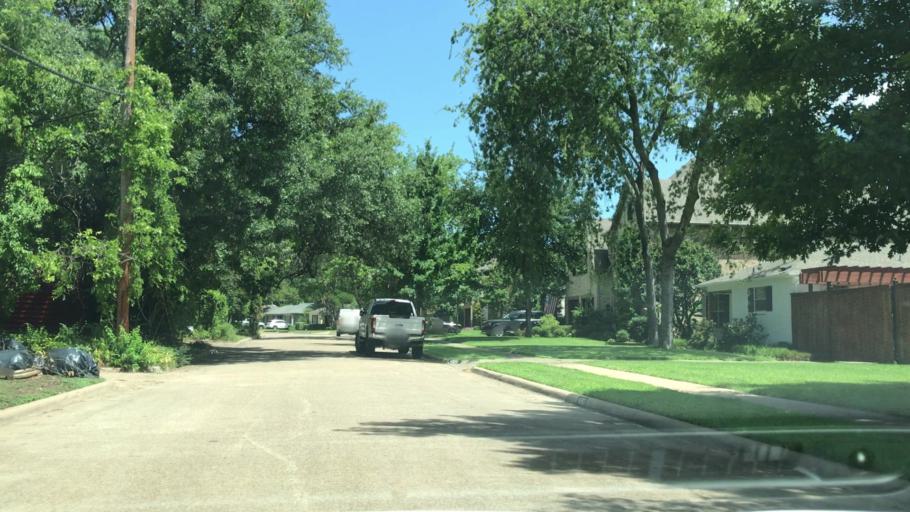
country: US
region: Texas
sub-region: Dallas County
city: University Park
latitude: 32.8731
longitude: -96.8444
